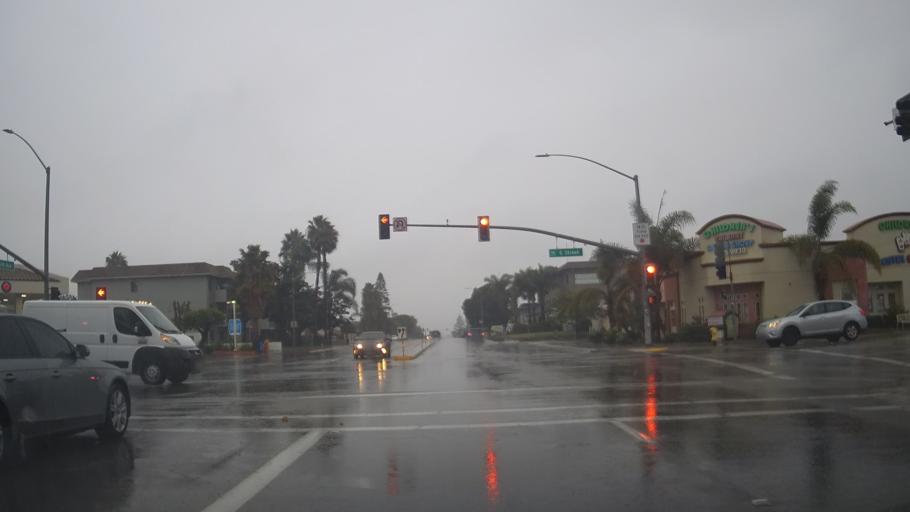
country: US
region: California
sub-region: San Diego County
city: Chula Vista
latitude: 32.6430
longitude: -117.0850
